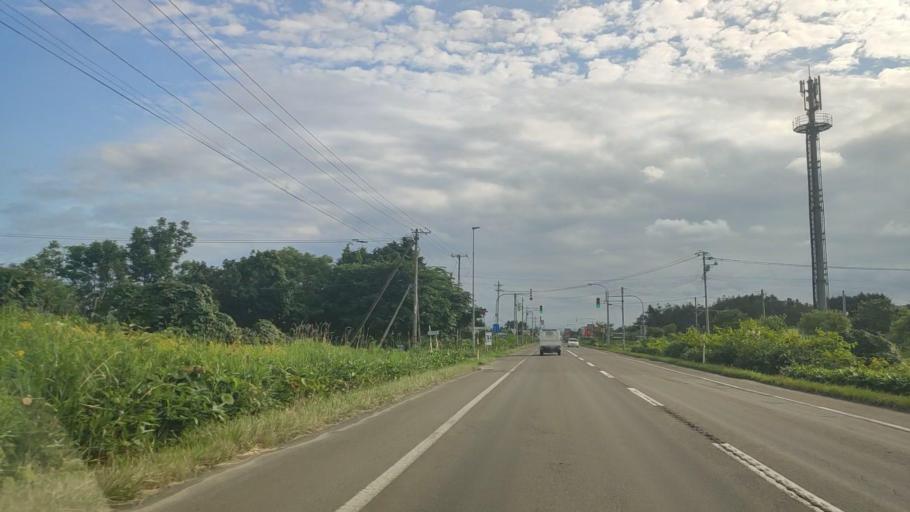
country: JP
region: Hokkaido
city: Niseko Town
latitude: 42.4821
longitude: 140.3513
